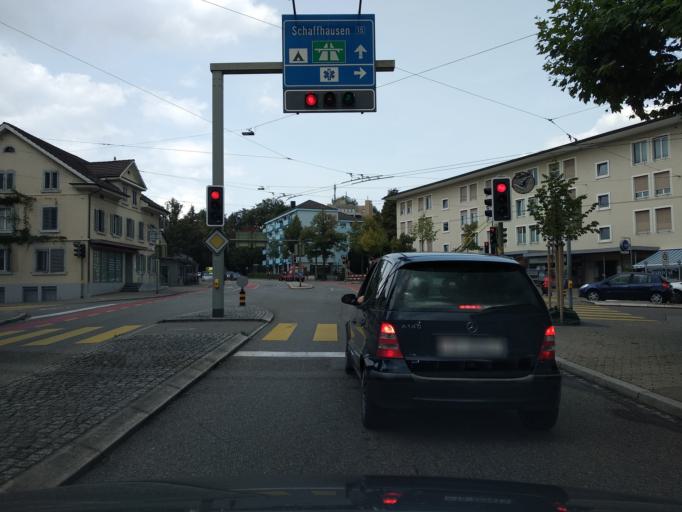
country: CH
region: Zurich
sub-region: Bezirk Winterthur
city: Veltheim (Kreis 5) / Blumenau
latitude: 47.5089
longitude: 8.7230
